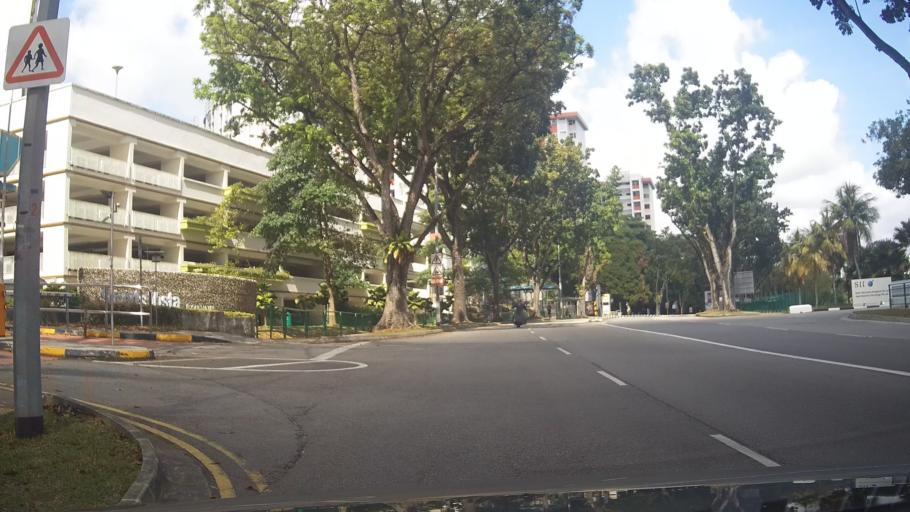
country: MY
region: Johor
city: Johor Bahru
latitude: 1.4417
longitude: 103.7790
